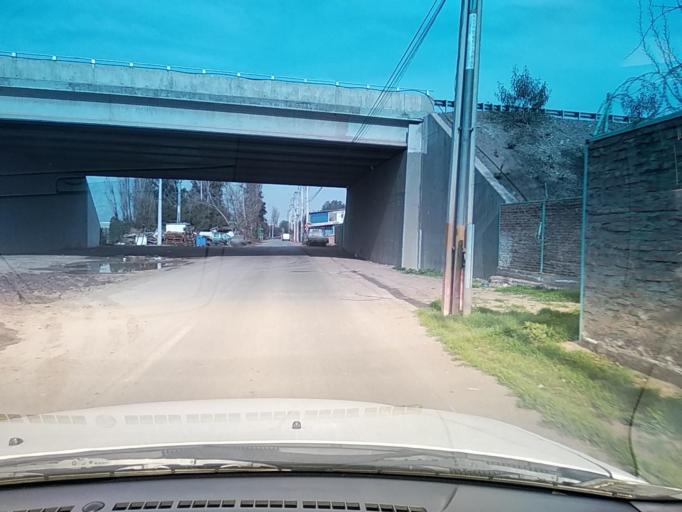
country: CL
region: Santiago Metropolitan
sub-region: Provincia de Chacabuco
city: Chicureo Abajo
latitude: -33.2962
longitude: -70.7233
